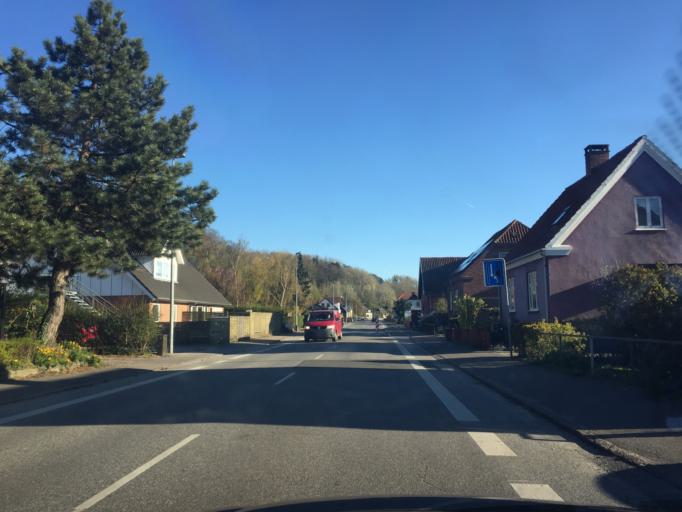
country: DK
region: Capital Region
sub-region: Halsnaes Kommune
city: Frederiksvaerk
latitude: 55.9656
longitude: 12.0210
